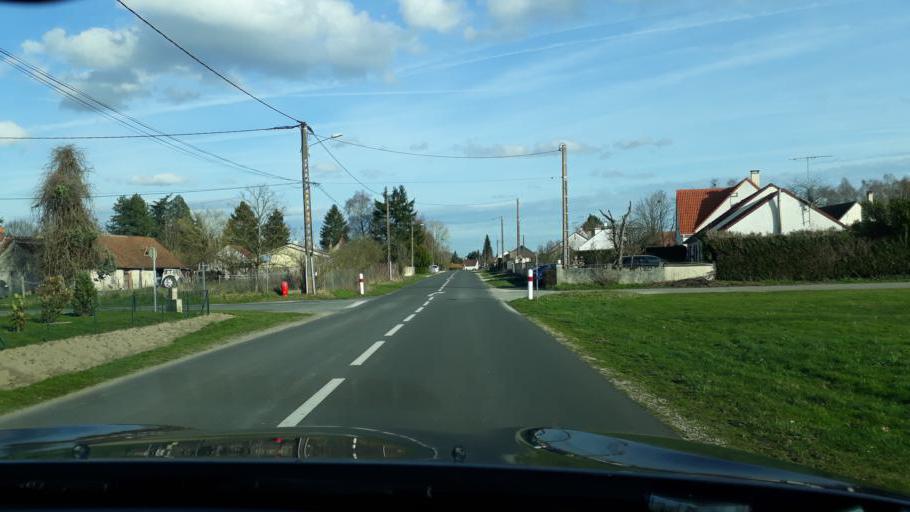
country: FR
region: Centre
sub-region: Departement du Loiret
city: Chilleurs-aux-Bois
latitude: 48.0561
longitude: 2.1878
